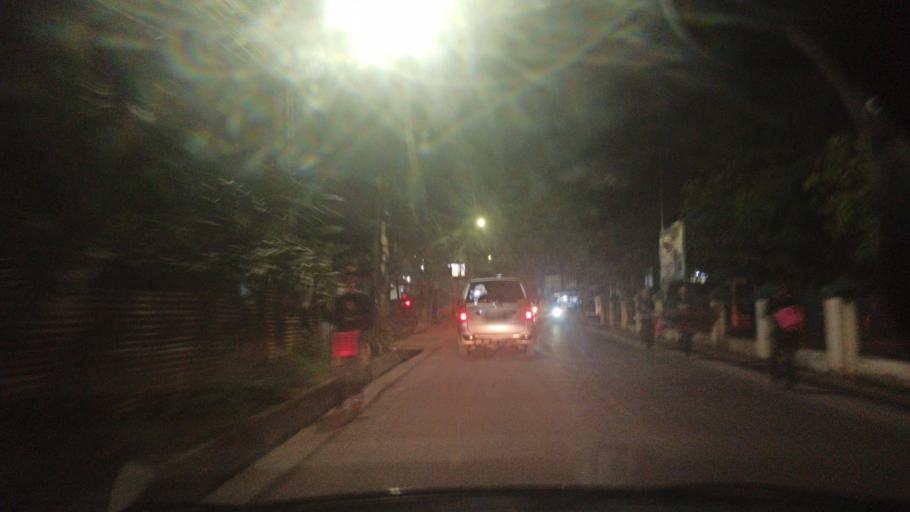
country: ID
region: South Sumatra
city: Palembang
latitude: -2.9271
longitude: 104.7867
